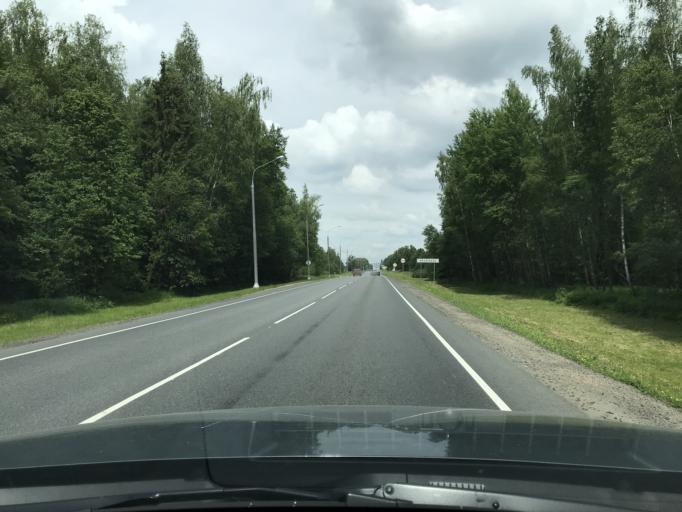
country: RU
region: Kaluga
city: Borovsk
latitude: 55.3709
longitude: 36.4112
